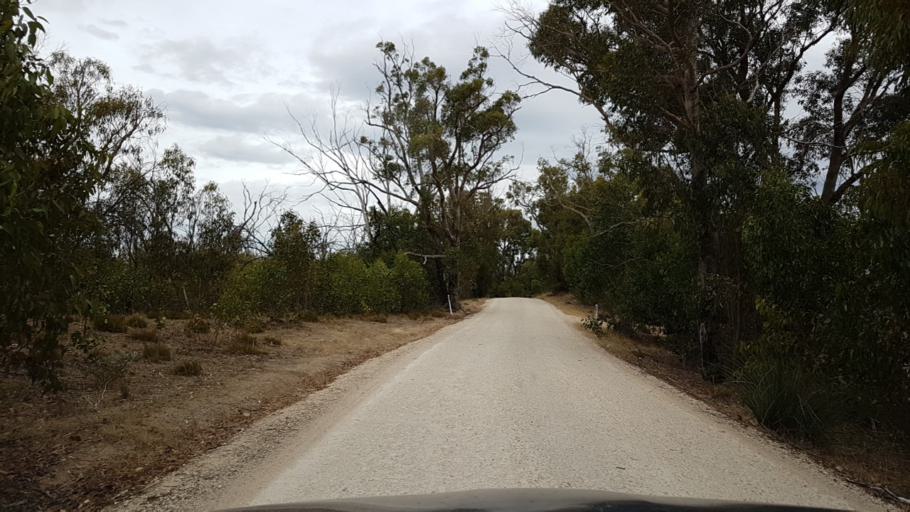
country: AU
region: South Australia
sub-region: Tea Tree Gully
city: Golden Grove
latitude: -34.7763
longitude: 138.8134
